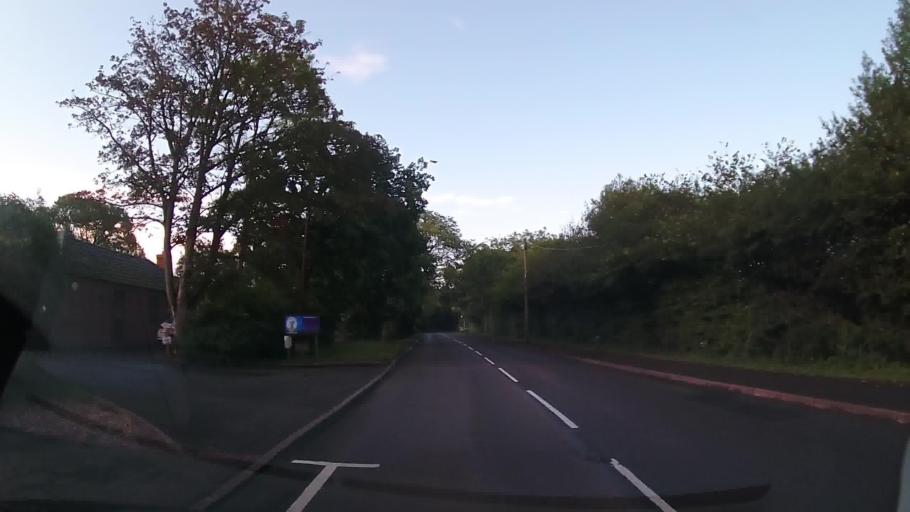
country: GB
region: England
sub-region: Leicestershire
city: Markfield
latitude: 52.6770
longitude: -1.2746
